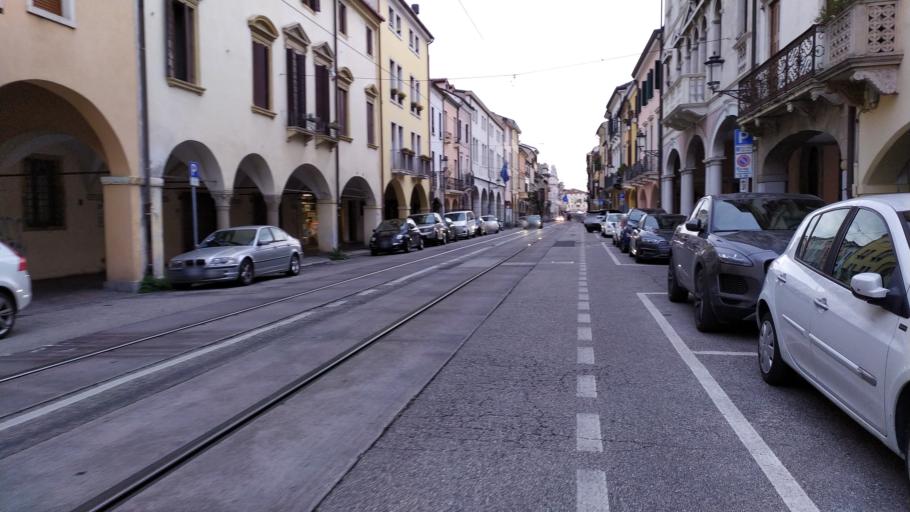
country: IT
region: Veneto
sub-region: Provincia di Padova
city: Padova
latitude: 45.3961
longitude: 11.8735
